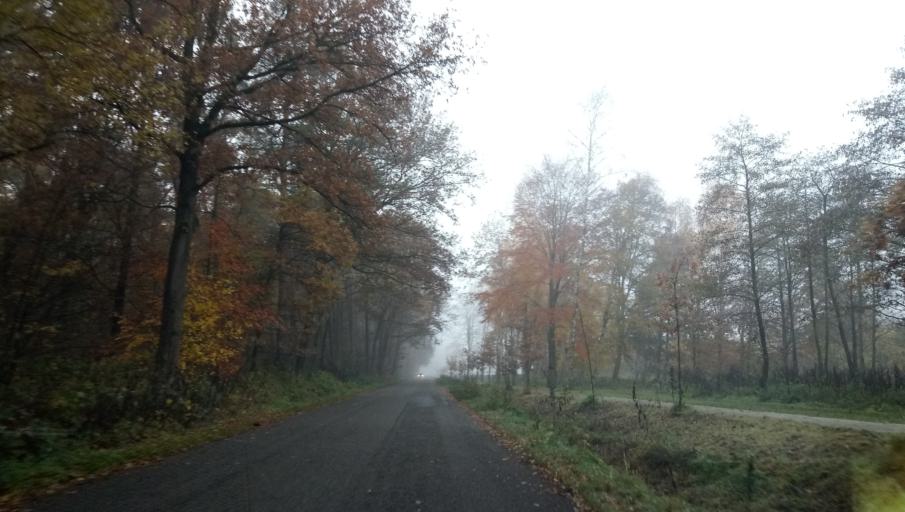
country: NL
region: Gelderland
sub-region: Gemeente Voorst
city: Twello
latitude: 52.1933
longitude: 6.0996
